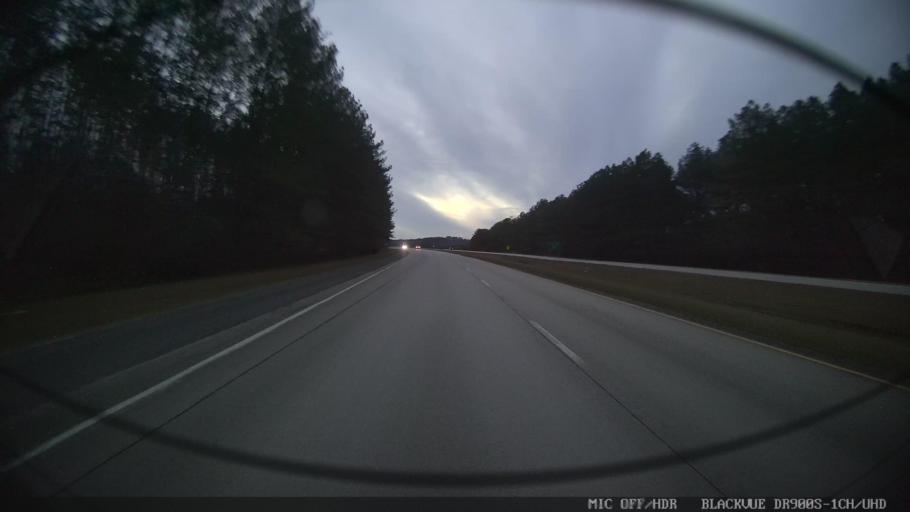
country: US
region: Mississippi
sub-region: Lauderdale County
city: Meridian
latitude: 32.3343
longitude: -88.6570
